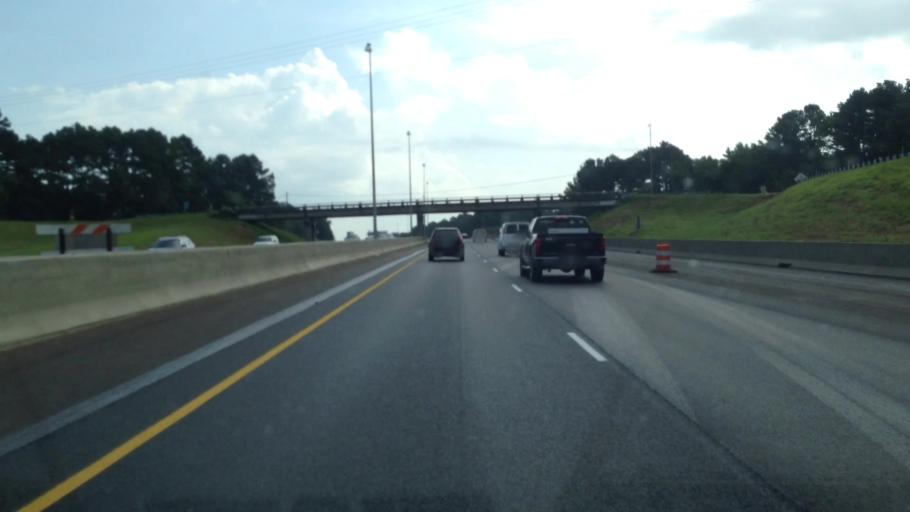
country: US
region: Mississippi
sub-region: Hinds County
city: Byram
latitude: 32.2088
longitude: -90.2371
